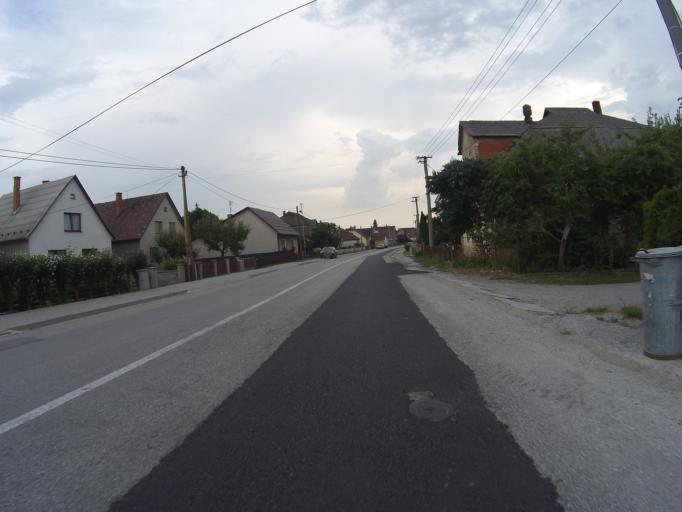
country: SK
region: Nitriansky
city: Ilava
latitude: 49.0410
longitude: 18.2913
